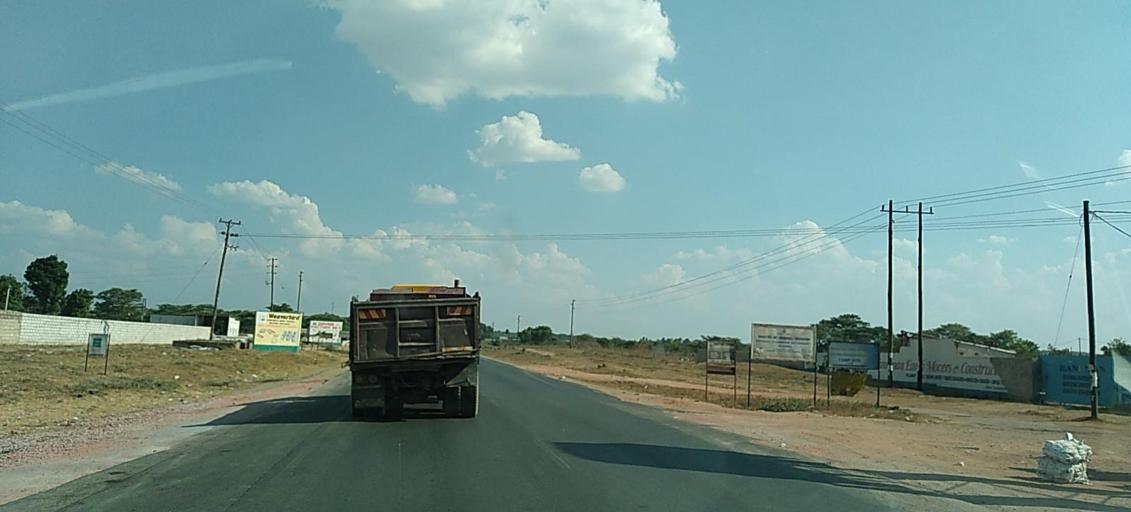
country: ZM
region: Lusaka
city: Lusaka
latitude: -15.2391
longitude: 28.2574
